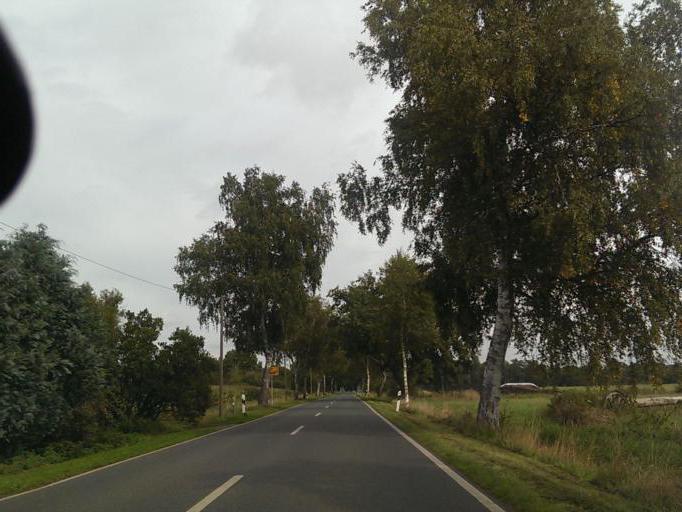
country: DE
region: Lower Saxony
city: Garbsen-Mitte
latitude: 52.4747
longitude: 9.6222
